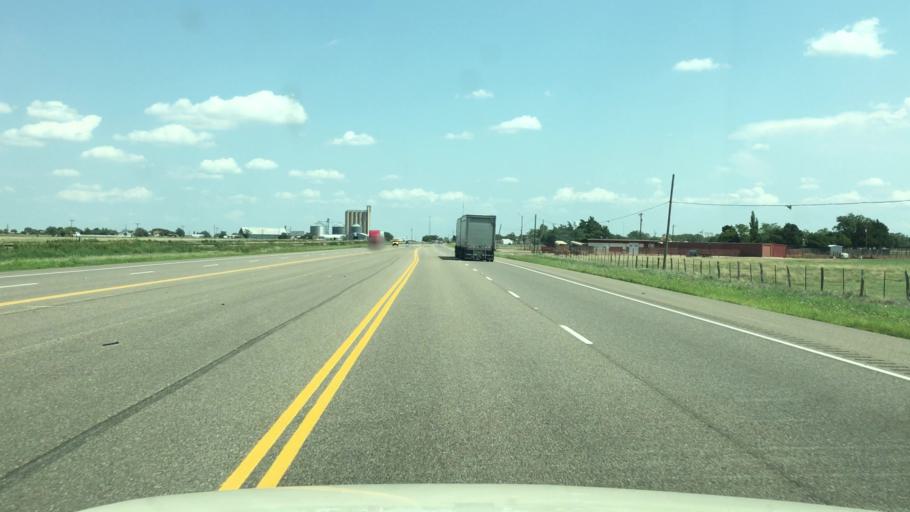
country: US
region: Texas
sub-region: Armstrong County
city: Claude
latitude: 35.1162
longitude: -101.3727
